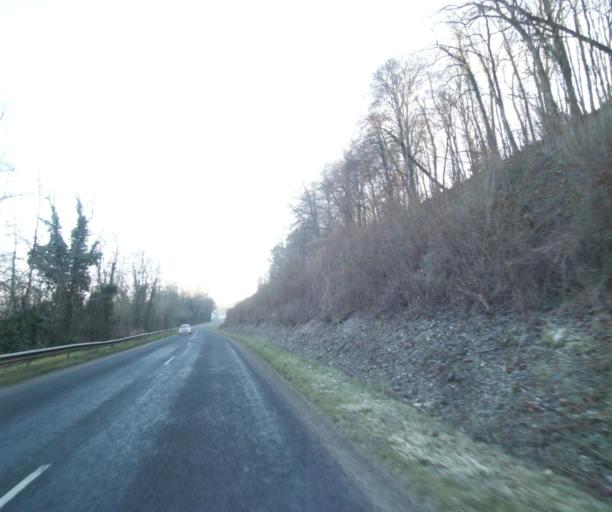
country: FR
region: Champagne-Ardenne
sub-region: Departement de la Haute-Marne
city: Bienville
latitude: 48.5529
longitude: 5.0682
